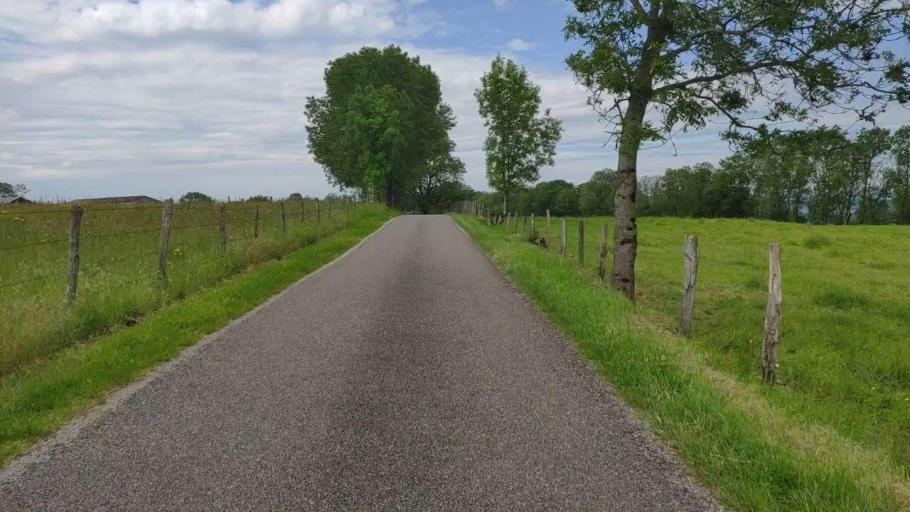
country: FR
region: Franche-Comte
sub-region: Departement du Jura
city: Poligny
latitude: 46.7603
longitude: 5.6379
